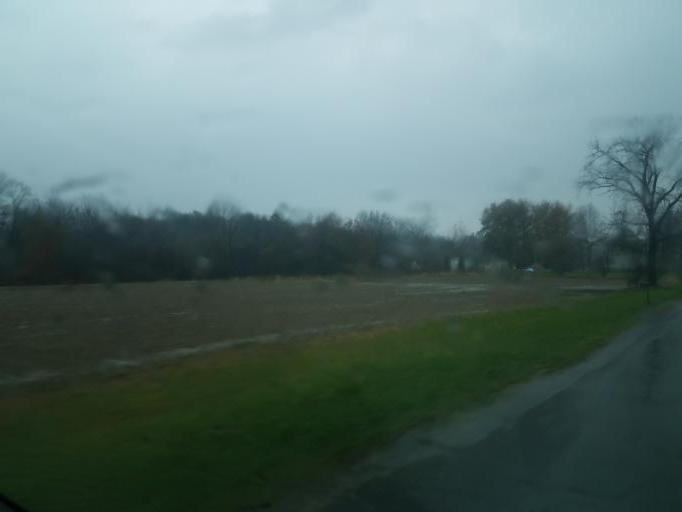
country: US
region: Ohio
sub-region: Delaware County
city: Ashley
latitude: 40.4182
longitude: -82.8995
